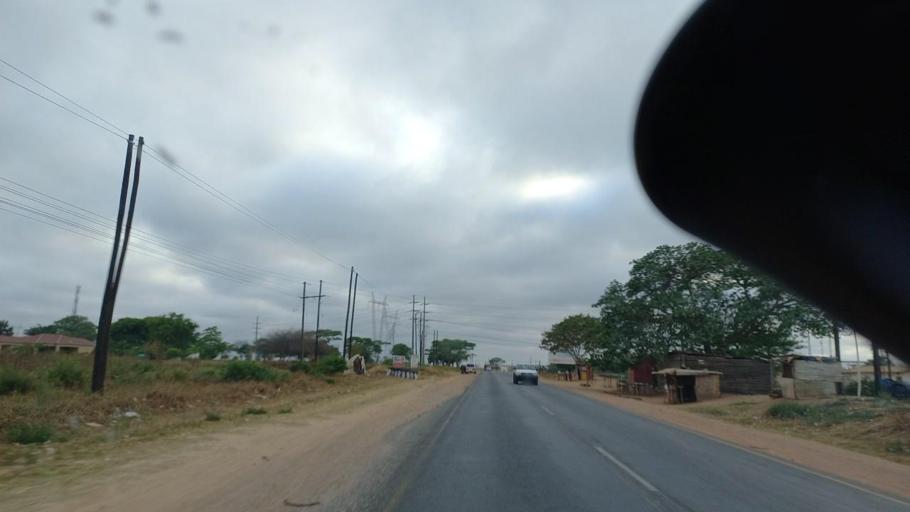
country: ZM
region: Lusaka
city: Chongwe
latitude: -15.3436
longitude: 28.5145
